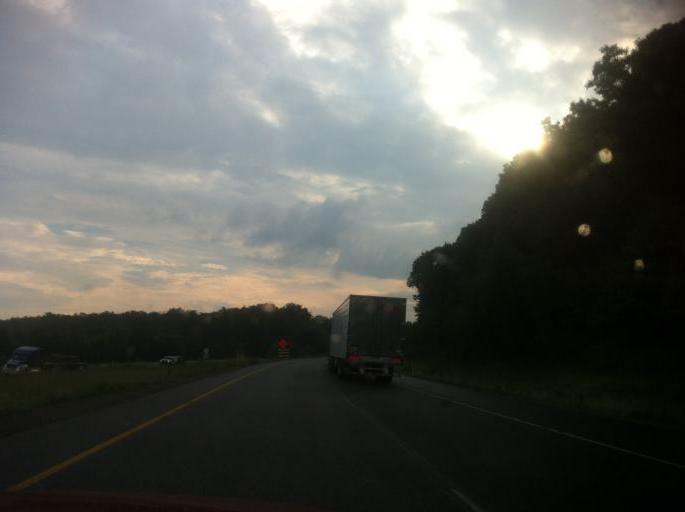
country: US
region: Pennsylvania
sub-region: Clarion County
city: Marianne
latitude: 41.1971
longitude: -79.4736
